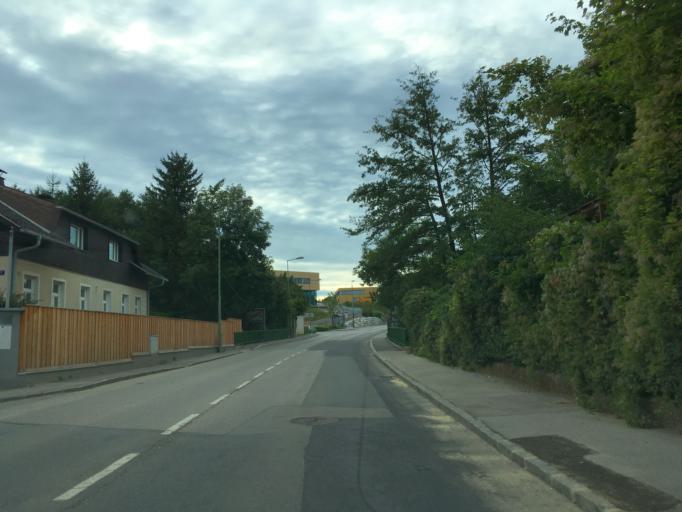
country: AT
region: Lower Austria
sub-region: Politischer Bezirk Tulln
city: Wordern
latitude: 48.3083
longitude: 16.2593
